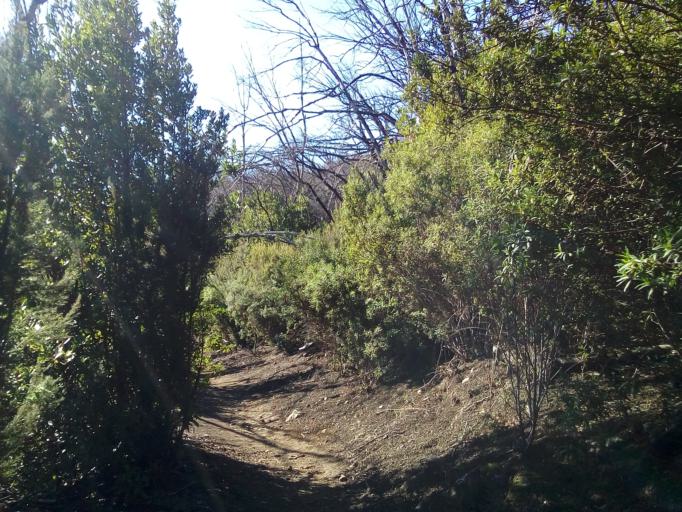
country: ES
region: Canary Islands
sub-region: Provincia de Santa Cruz de Tenerife
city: Vallehermosa
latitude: 28.1235
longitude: -17.2630
